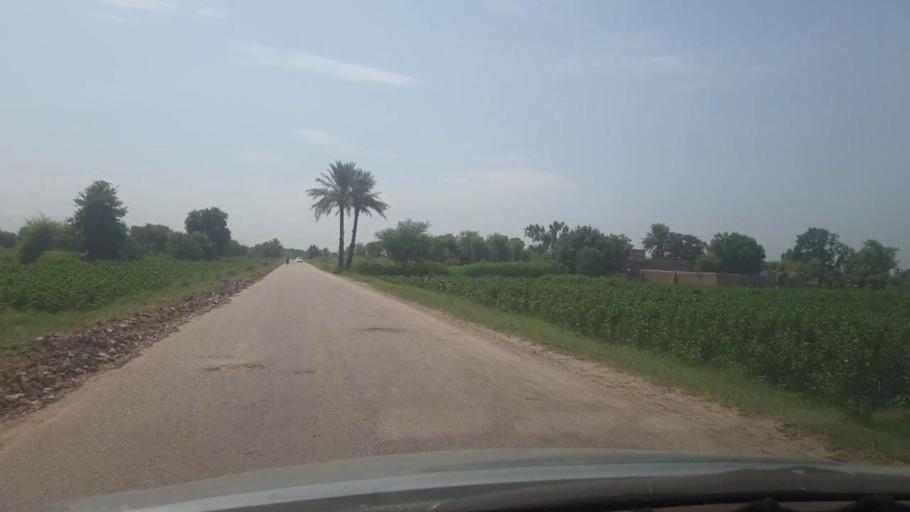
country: PK
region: Sindh
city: Bozdar
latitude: 27.2146
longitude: 68.5726
